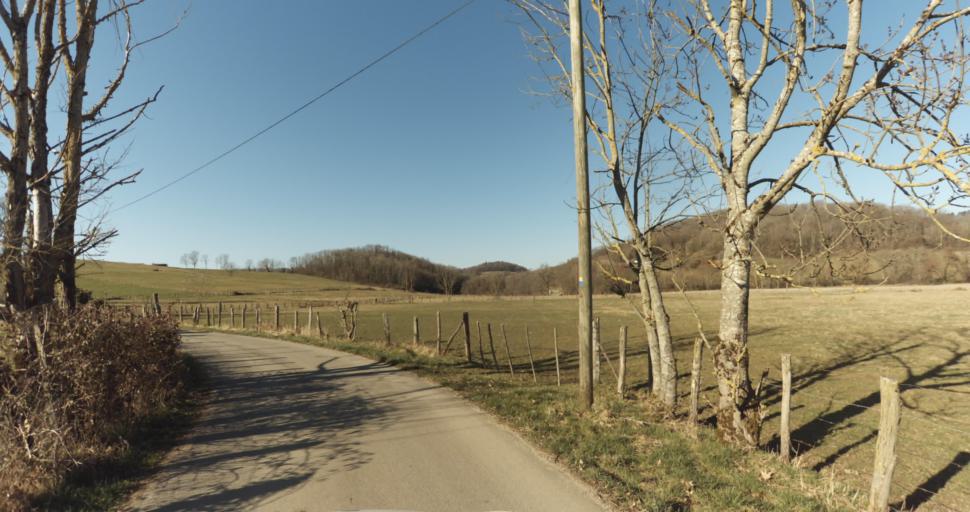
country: FR
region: Franche-Comte
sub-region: Departement du Jura
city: Montmorot
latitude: 46.6996
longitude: 5.5300
